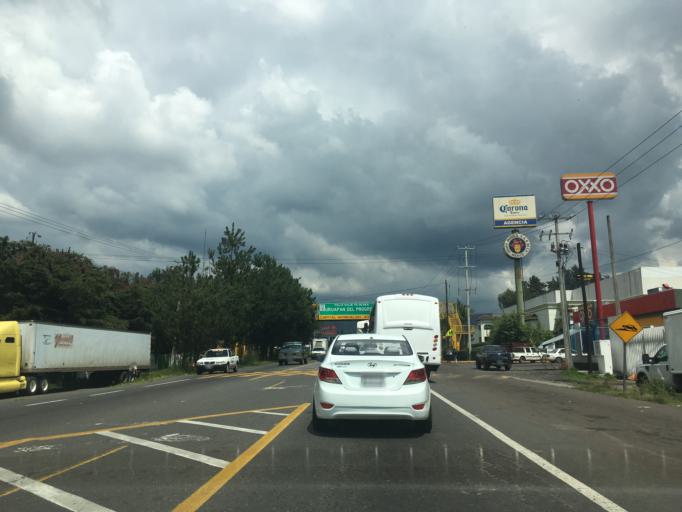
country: MX
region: Michoacan
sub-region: Uruapan
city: Uruapan
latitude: 19.4728
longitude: -102.0729
